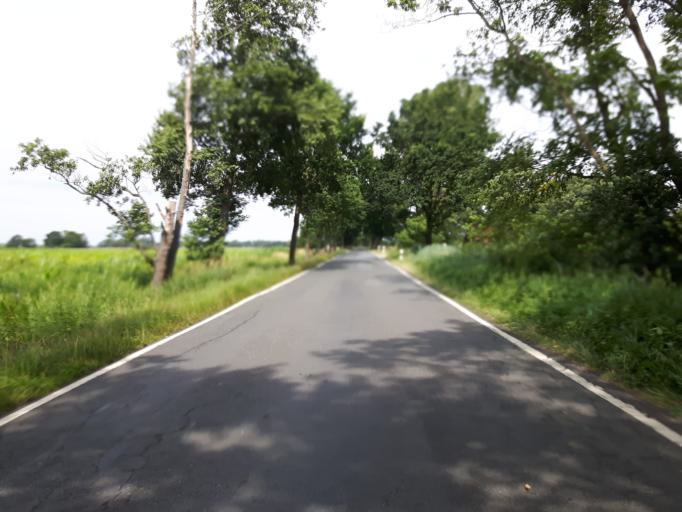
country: DE
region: Lower Saxony
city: Rastede
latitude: 53.3311
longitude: 8.2583
